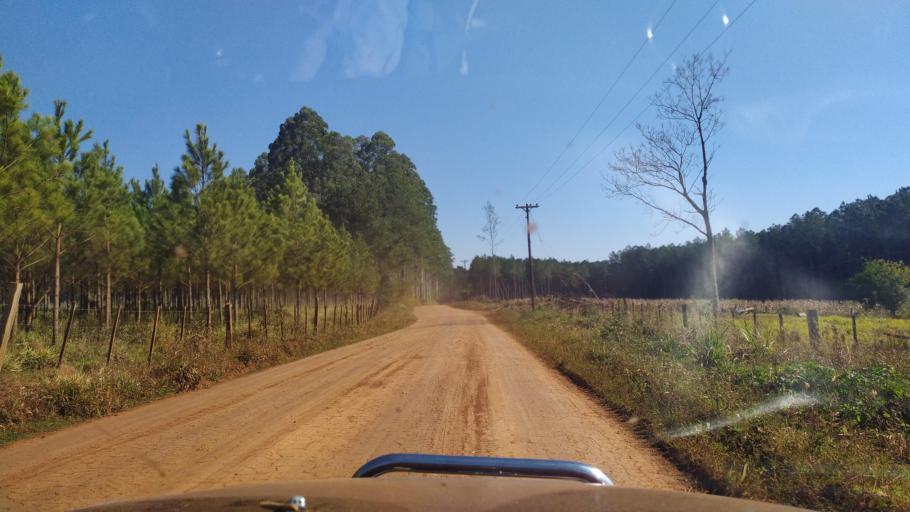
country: AR
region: Misiones
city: El Alcazar
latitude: -26.7148
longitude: -54.7045
